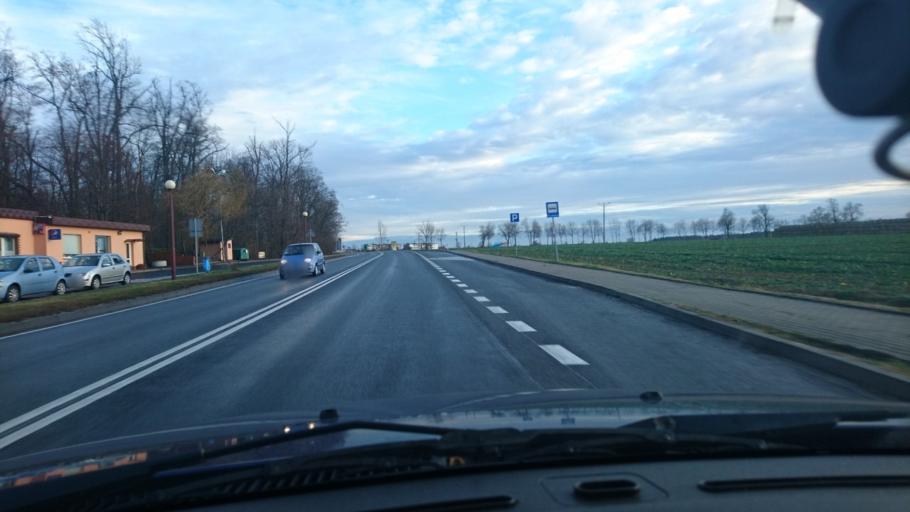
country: PL
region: Greater Poland Voivodeship
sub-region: Powiat kepinski
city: Slupia pod Kepnem
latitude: 51.2410
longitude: 18.0339
